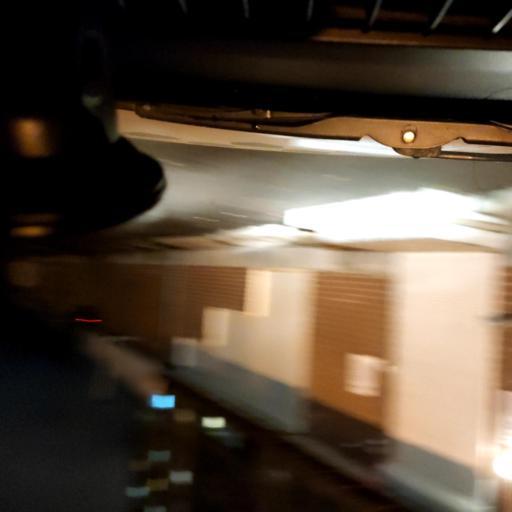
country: RU
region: Perm
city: Perm
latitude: 57.9920
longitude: 56.2265
